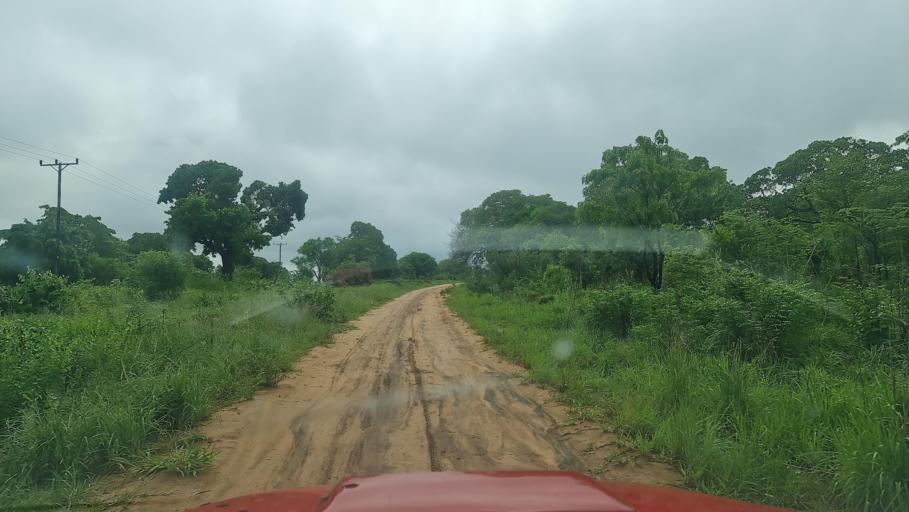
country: MW
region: Southern Region
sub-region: Nsanje District
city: Nsanje
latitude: -17.1926
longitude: 35.8524
